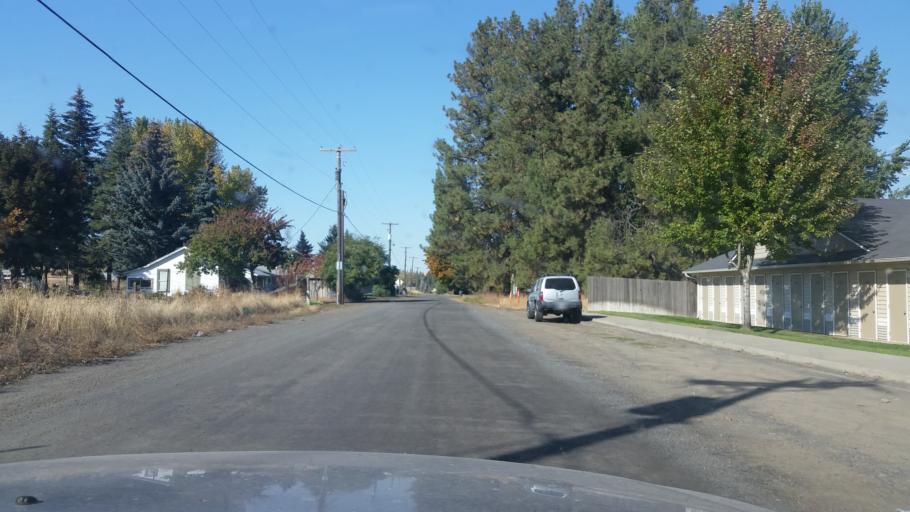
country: US
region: Washington
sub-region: Spokane County
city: Cheney
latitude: 47.5079
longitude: -117.5702
